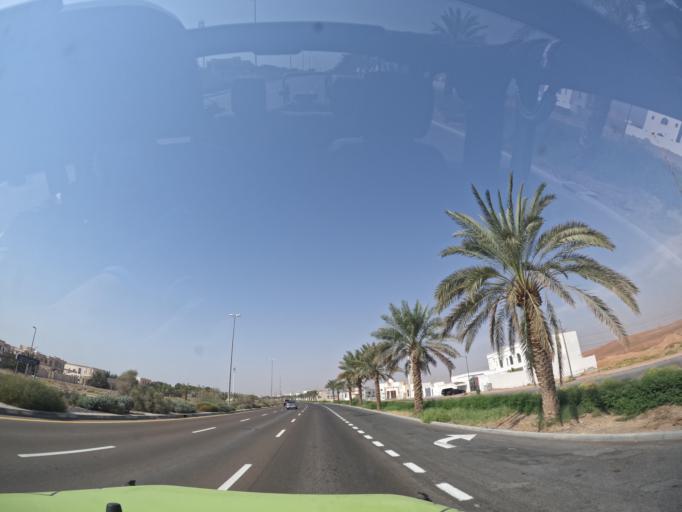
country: OM
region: Al Buraimi
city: Al Buraymi
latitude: 24.2680
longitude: 55.7010
